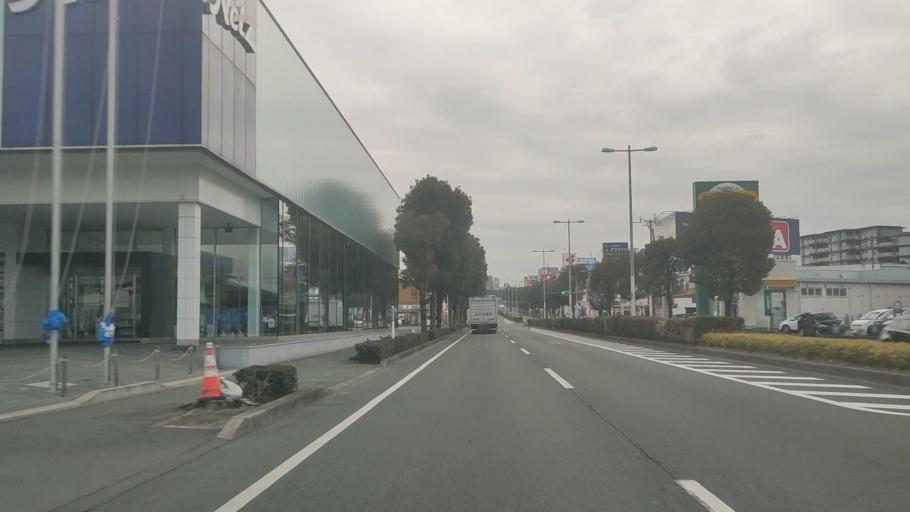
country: JP
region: Kumamoto
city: Kumamoto
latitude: 32.8184
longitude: 130.7543
